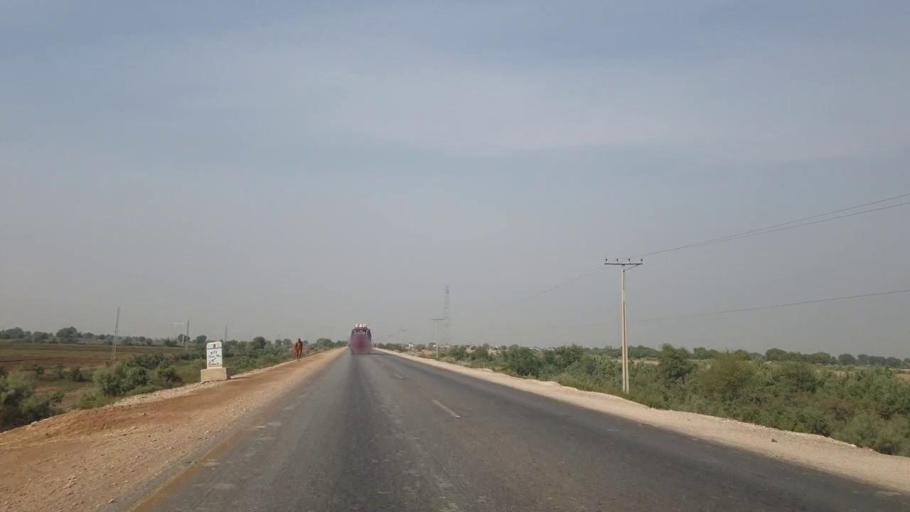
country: PK
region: Sindh
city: Sann
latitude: 26.0796
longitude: 68.0950
